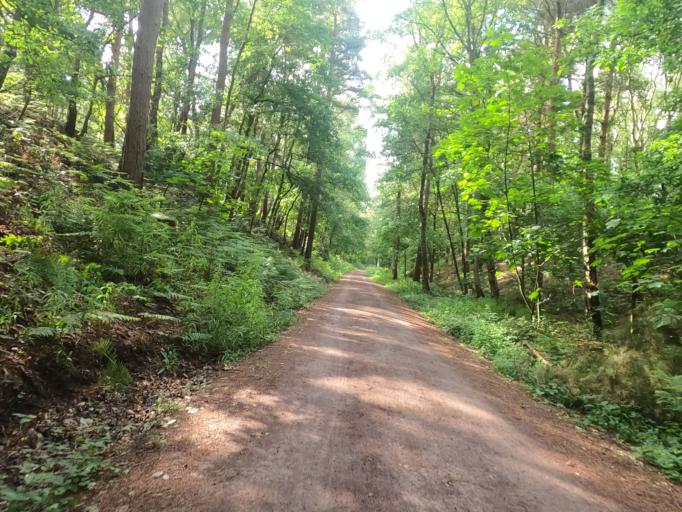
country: GB
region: England
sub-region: Cheshire West and Chester
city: Cuddington
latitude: 53.2185
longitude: -2.6098
